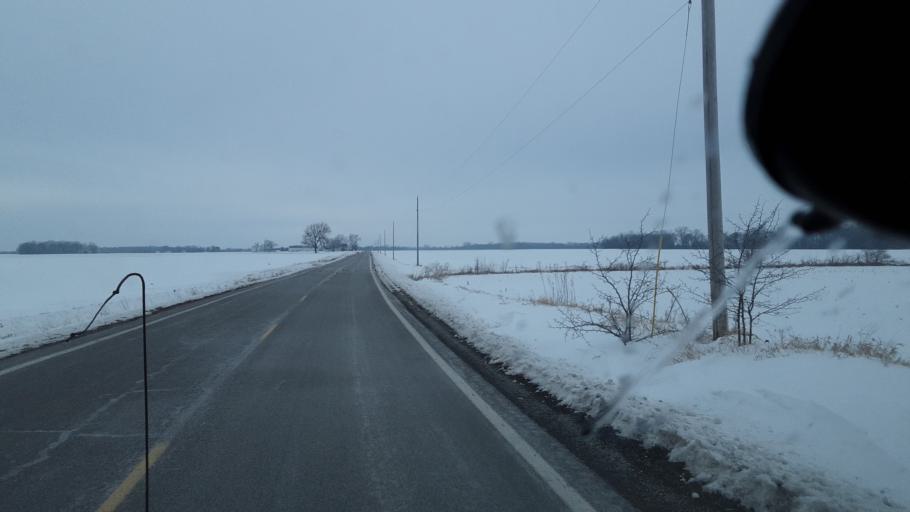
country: US
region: Ohio
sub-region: Union County
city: Marysville
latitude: 40.1156
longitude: -83.4269
